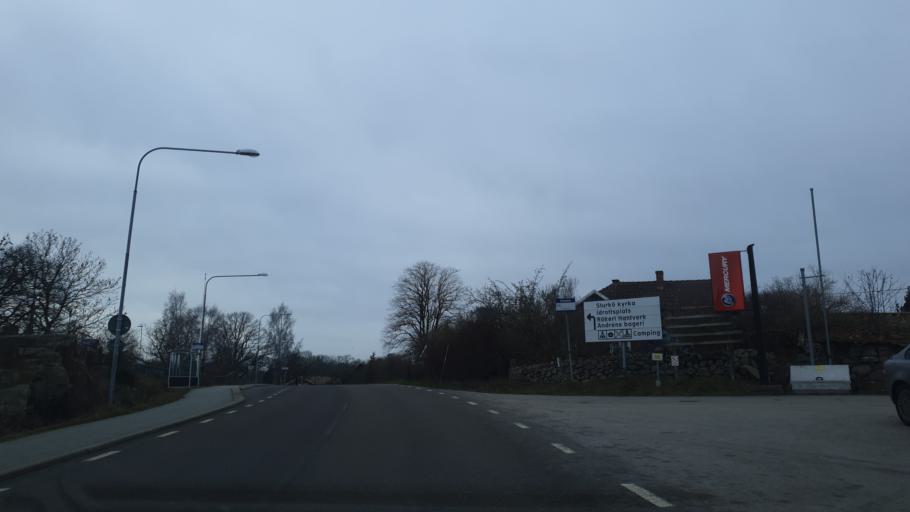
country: SE
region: Blekinge
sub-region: Karlskrona Kommun
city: Sturko
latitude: 56.1132
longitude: 15.6820
